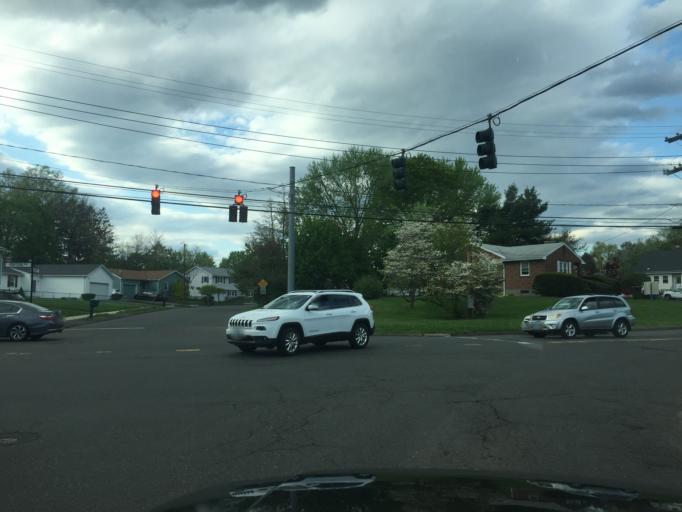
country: US
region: Connecticut
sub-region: Hartford County
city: Kensington
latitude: 41.6316
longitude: -72.7544
